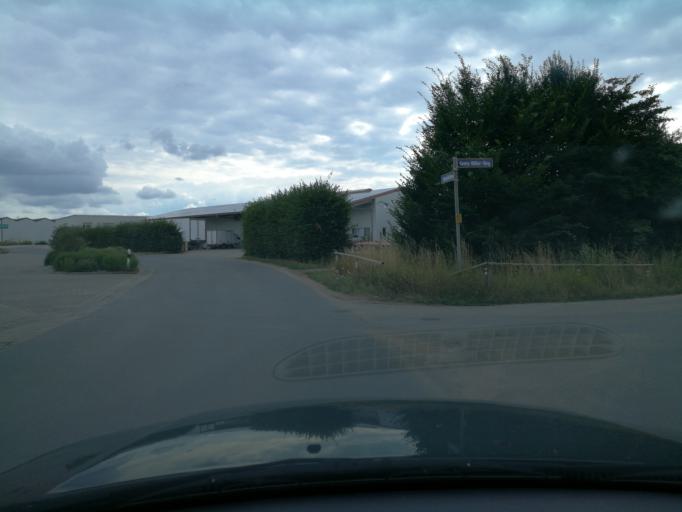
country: DE
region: Bavaria
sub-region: Regierungsbezirk Mittelfranken
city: Wetzendorf
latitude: 49.4844
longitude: 11.0470
